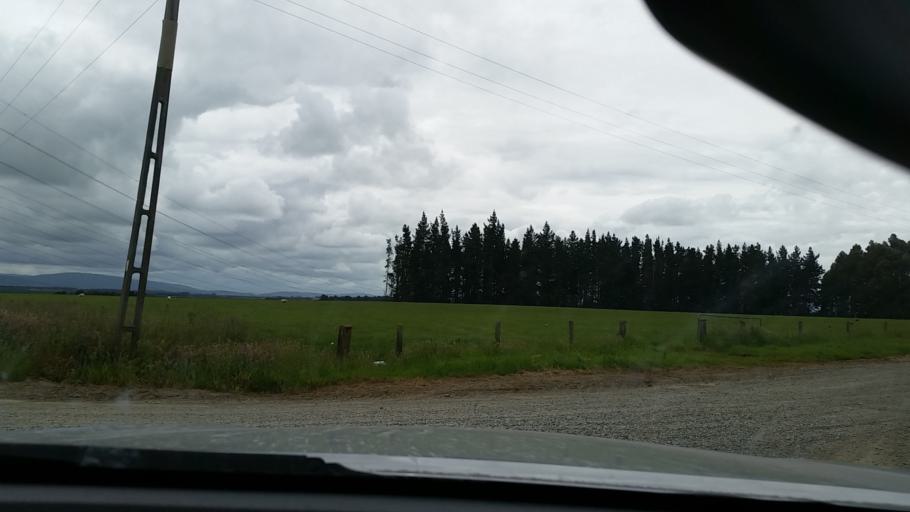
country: NZ
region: Southland
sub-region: Southland District
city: Winton
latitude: -46.1884
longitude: 168.1838
